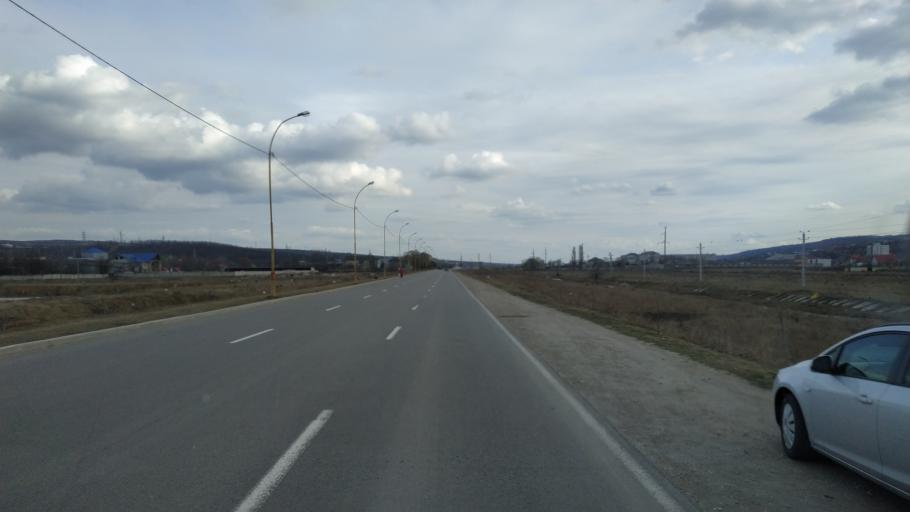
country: MD
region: Hincesti
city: Hincesti
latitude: 46.8294
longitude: 28.6005
